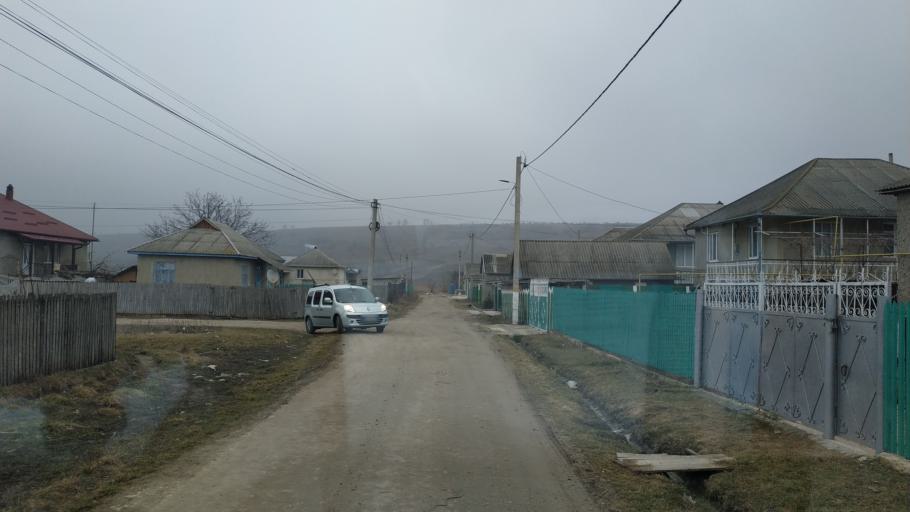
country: MD
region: Hincesti
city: Hincesti
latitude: 46.8910
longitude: 28.5471
